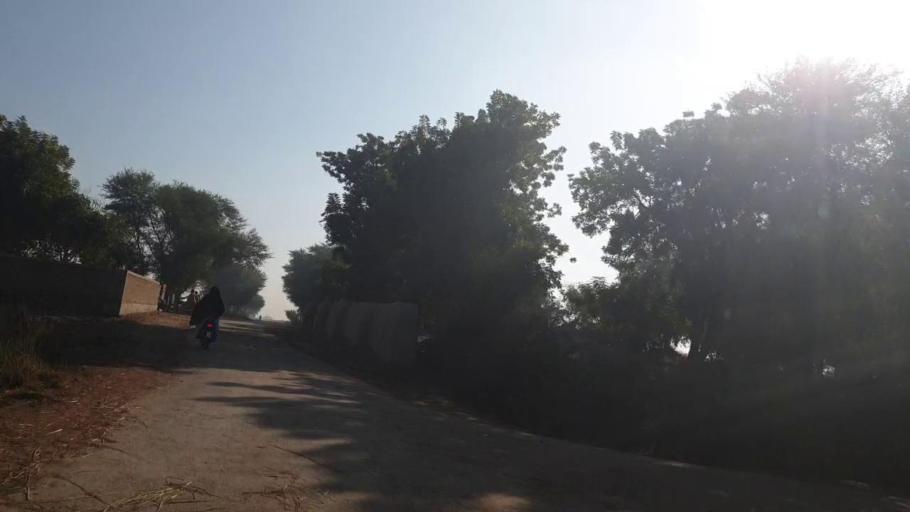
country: PK
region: Sindh
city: Dadu
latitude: 26.6738
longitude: 67.8094
